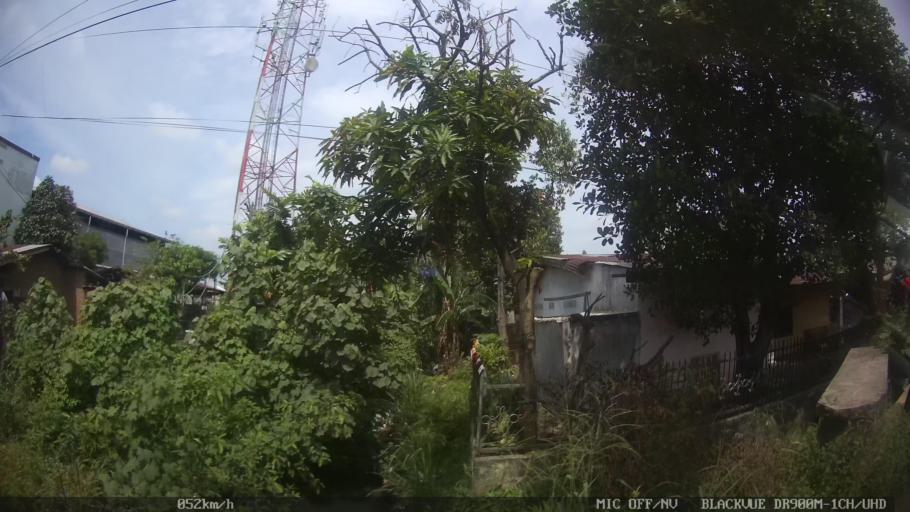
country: ID
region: North Sumatra
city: Medan
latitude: 3.6476
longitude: 98.7168
